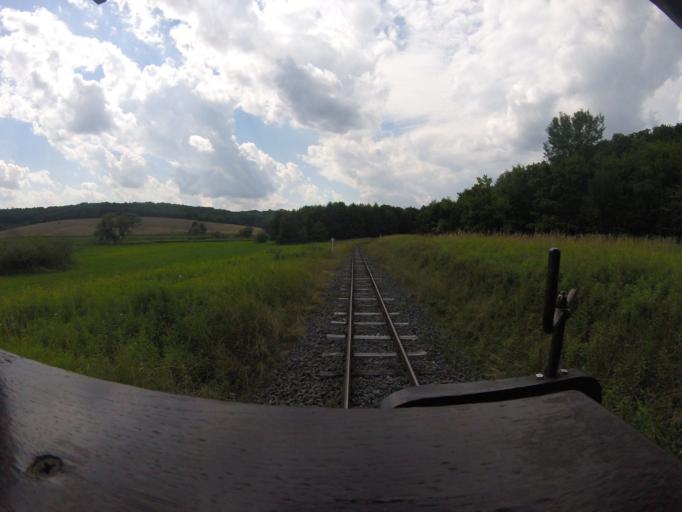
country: HU
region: Zala
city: Becsehely
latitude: 46.5417
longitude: 16.7297
